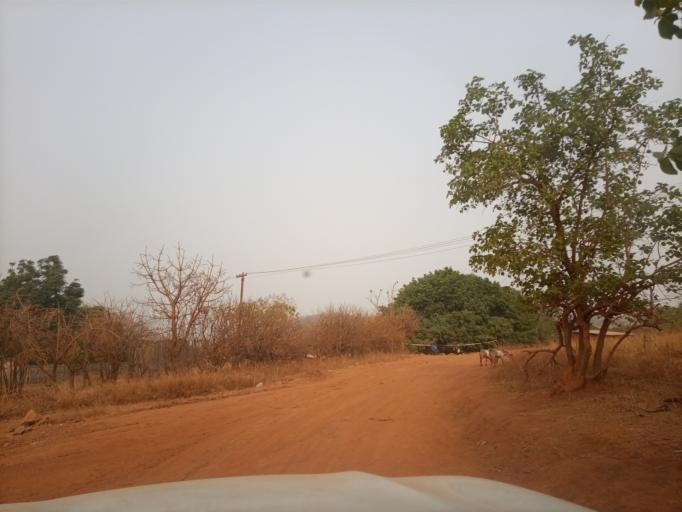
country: ET
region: Oromiya
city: Mendi
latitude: 10.2129
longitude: 35.0842
